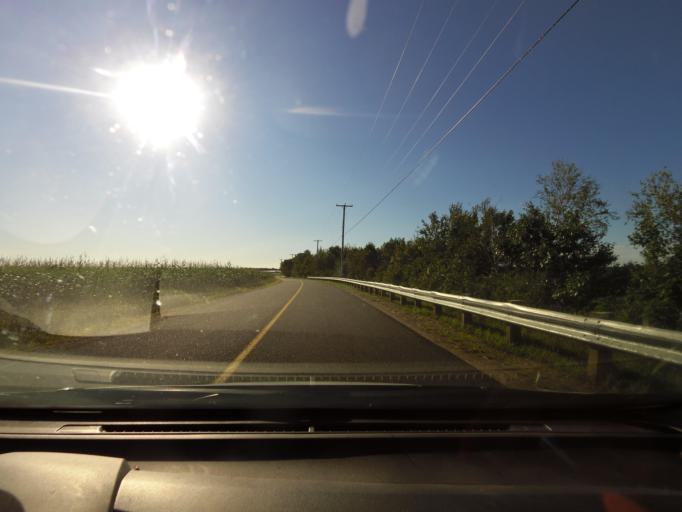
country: CA
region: Quebec
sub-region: Mauricie
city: Becancour
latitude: 46.5543
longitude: -72.3642
